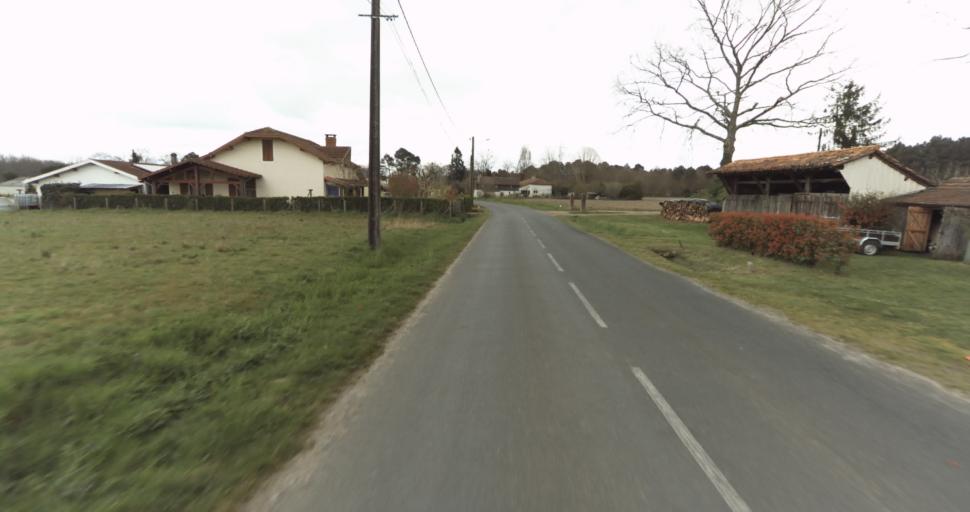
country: FR
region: Aquitaine
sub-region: Departement des Landes
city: Sarbazan
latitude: 44.0216
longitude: -0.3230
